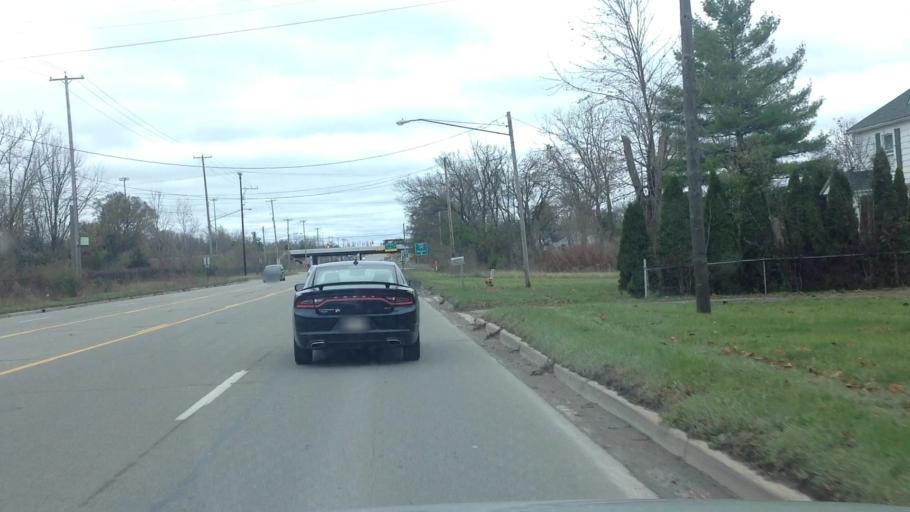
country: US
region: Michigan
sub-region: Genesee County
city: Beecher
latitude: 43.1027
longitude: -83.6944
